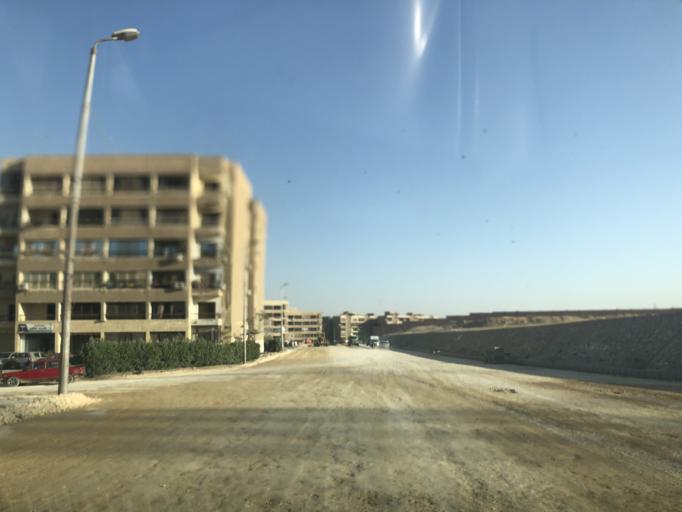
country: EG
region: Al Jizah
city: Al Jizah
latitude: 29.9884
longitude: 31.1118
